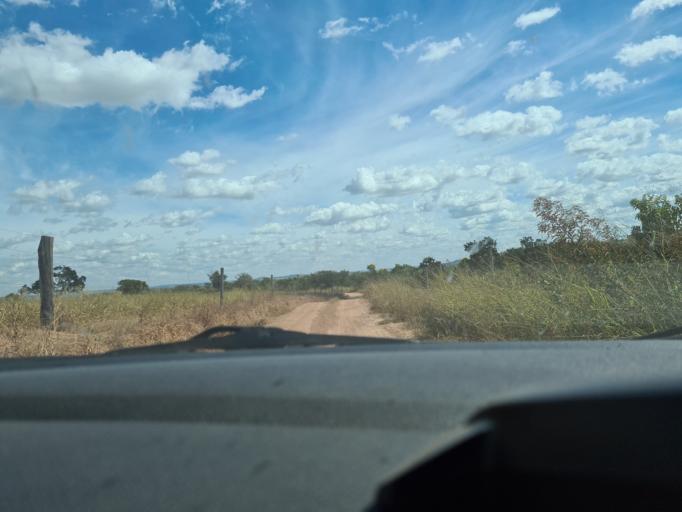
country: BR
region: Goias
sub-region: Silvania
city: Silvania
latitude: -16.5371
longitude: -48.5589
